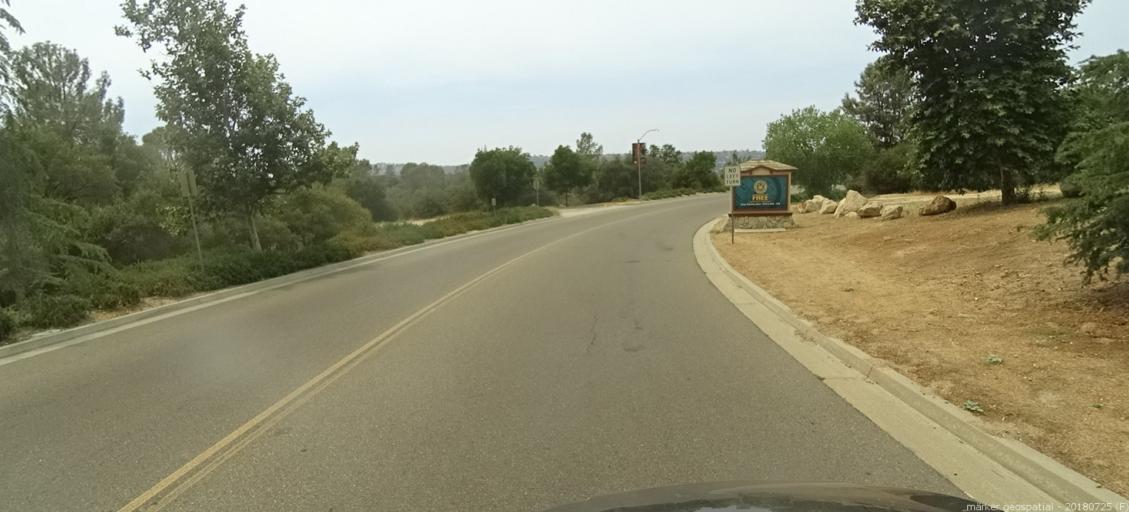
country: US
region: California
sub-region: Madera County
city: Coarsegold
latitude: 37.2112
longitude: -119.7047
